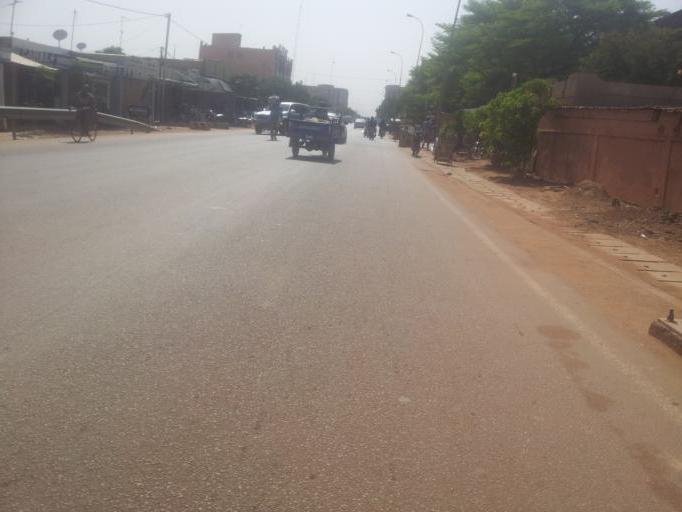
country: BF
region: Centre
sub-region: Kadiogo Province
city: Ouagadougou
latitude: 12.3771
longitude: -1.5349
